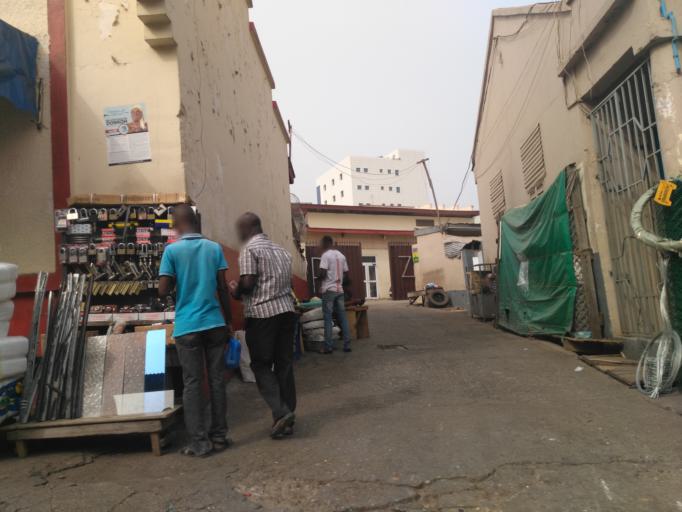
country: GH
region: Ashanti
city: Kumasi
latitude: 6.6968
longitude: -1.6228
